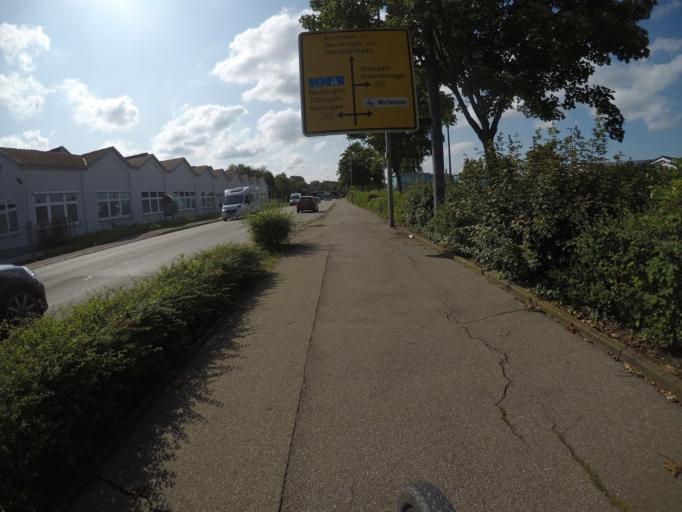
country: DE
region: Baden-Wuerttemberg
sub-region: Regierungsbezirk Stuttgart
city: Kongen
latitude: 48.6773
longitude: 9.3669
